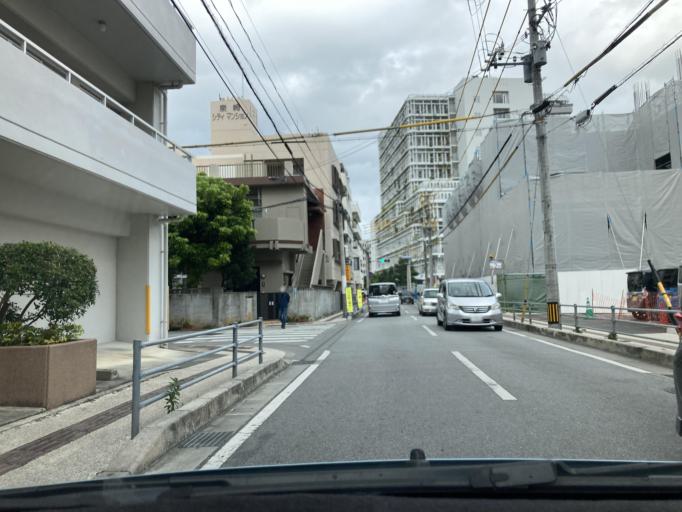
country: JP
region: Okinawa
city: Naha-shi
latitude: 26.2103
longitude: 127.6795
